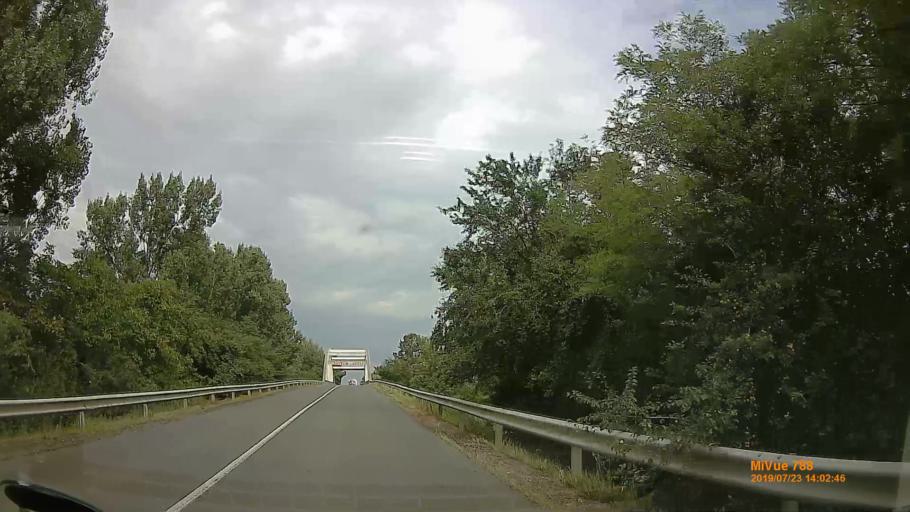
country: HU
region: Szabolcs-Szatmar-Bereg
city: Tiszavasvari
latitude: 47.9587
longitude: 21.3402
